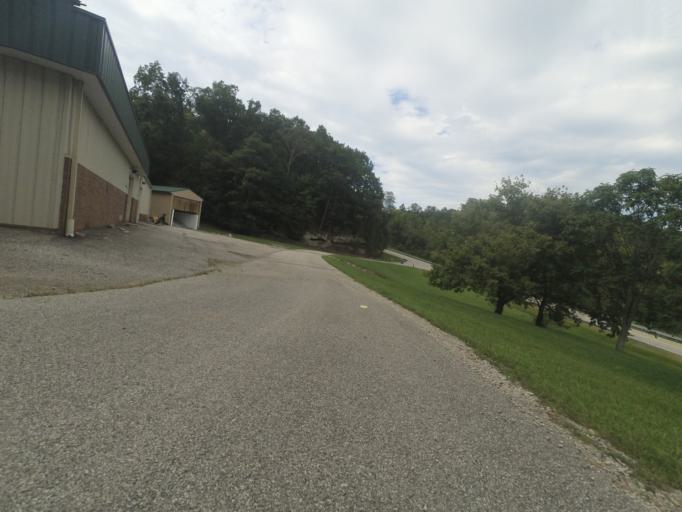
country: US
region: West Virginia
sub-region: Cabell County
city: Huntington
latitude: 38.3886
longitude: -82.4591
